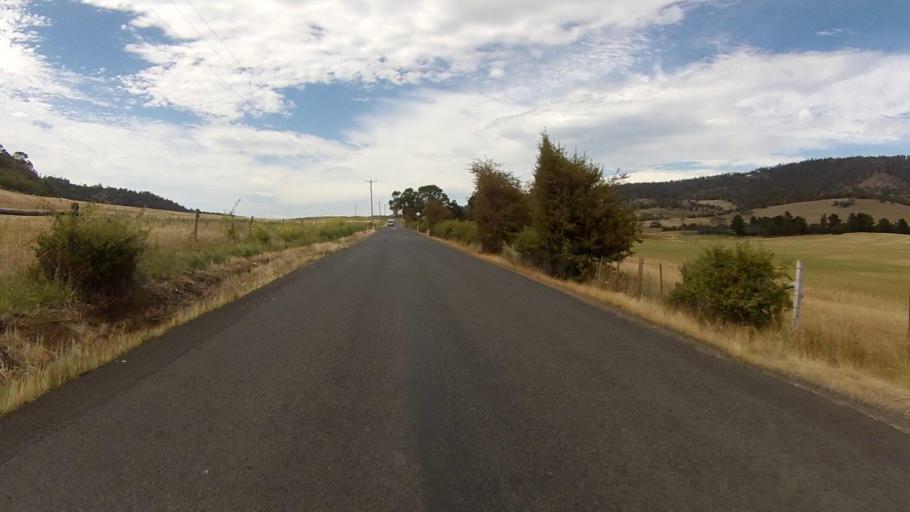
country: AU
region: Tasmania
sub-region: Brighton
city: Old Beach
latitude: -42.7251
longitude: 147.3425
